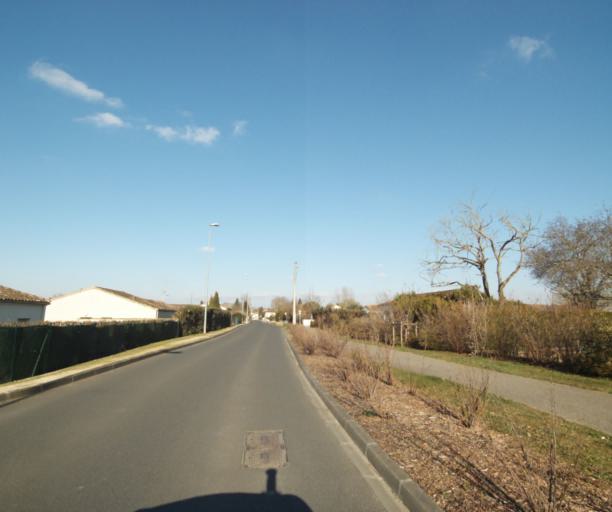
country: FR
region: Poitou-Charentes
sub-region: Departement des Deux-Sevres
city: Niort
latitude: 46.3420
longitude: -0.4582
